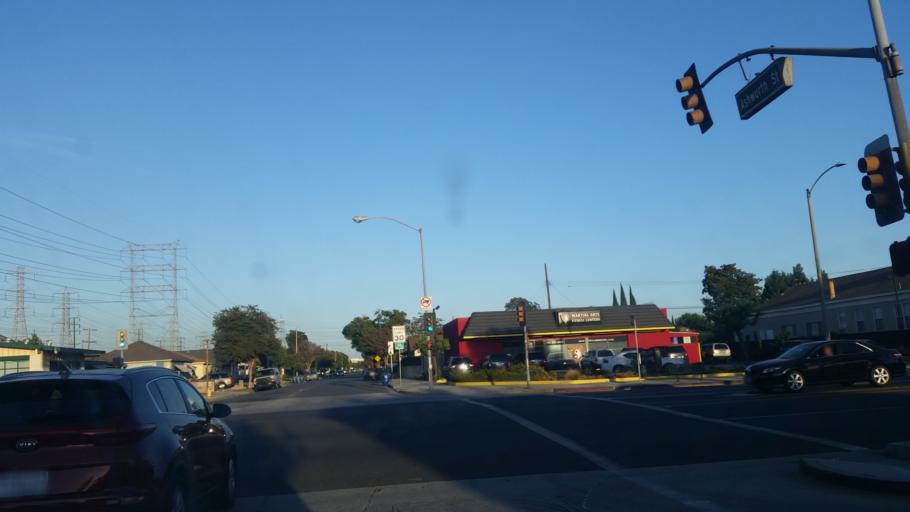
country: US
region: California
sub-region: Los Angeles County
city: Bellflower
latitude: 33.8679
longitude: -118.1254
